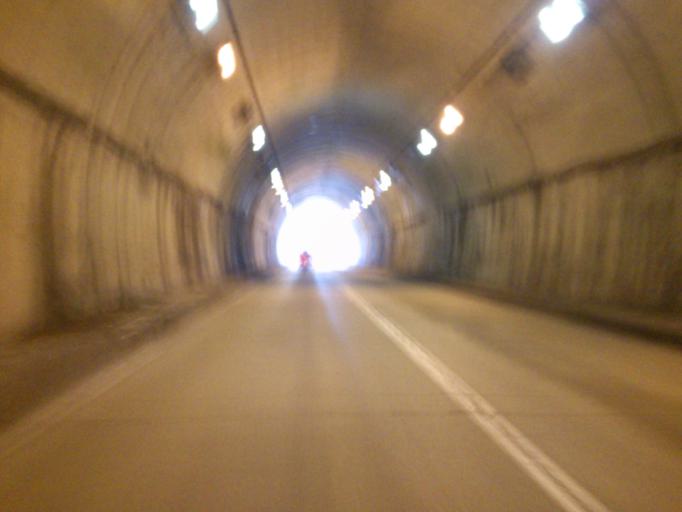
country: JP
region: Hyogo
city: Sasayama
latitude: 35.1434
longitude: 135.3395
